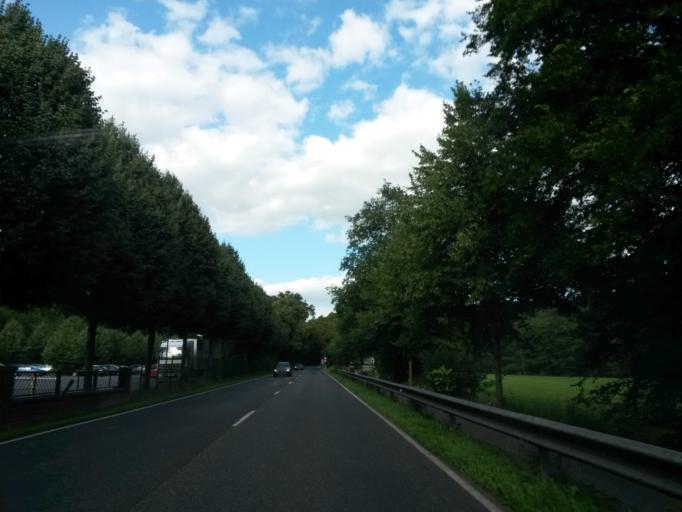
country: DE
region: North Rhine-Westphalia
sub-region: Regierungsbezirk Koln
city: Ruppichteroth
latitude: 50.8405
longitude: 7.4212
